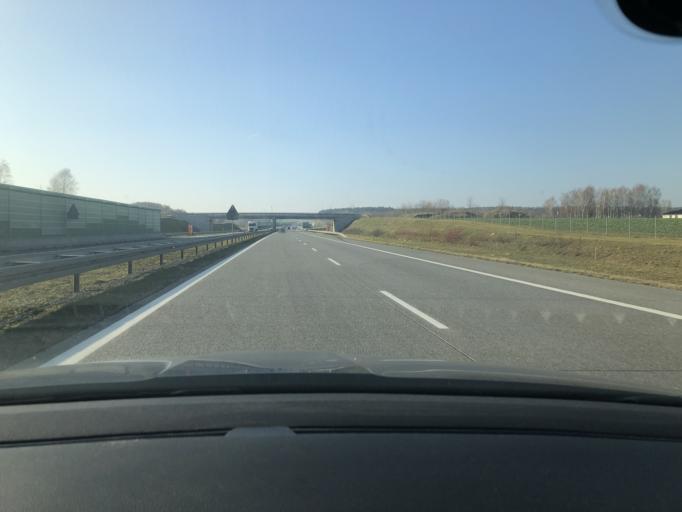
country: PL
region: Lubusz
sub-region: Powiat swiebodzinski
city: Lubrza
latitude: 52.3168
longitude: 15.4400
